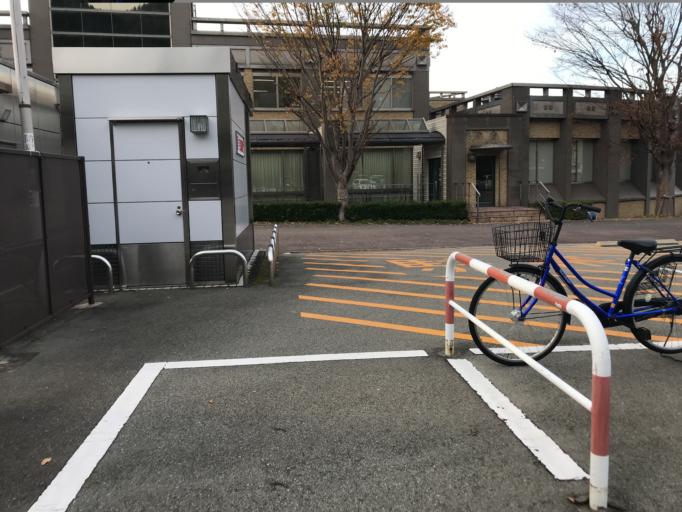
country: JP
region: Kyoto
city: Kameoka
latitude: 34.9958
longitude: 135.5541
